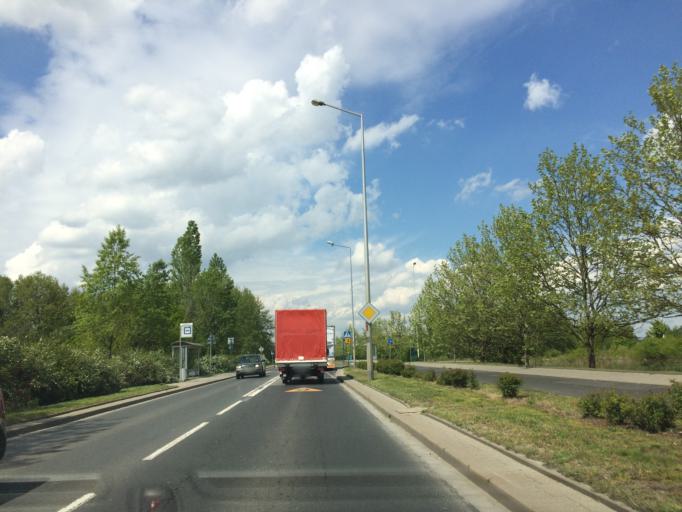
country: PL
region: Lower Silesian Voivodeship
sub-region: Powiat wroclawski
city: Smolec
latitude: 51.1515
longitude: 16.9275
